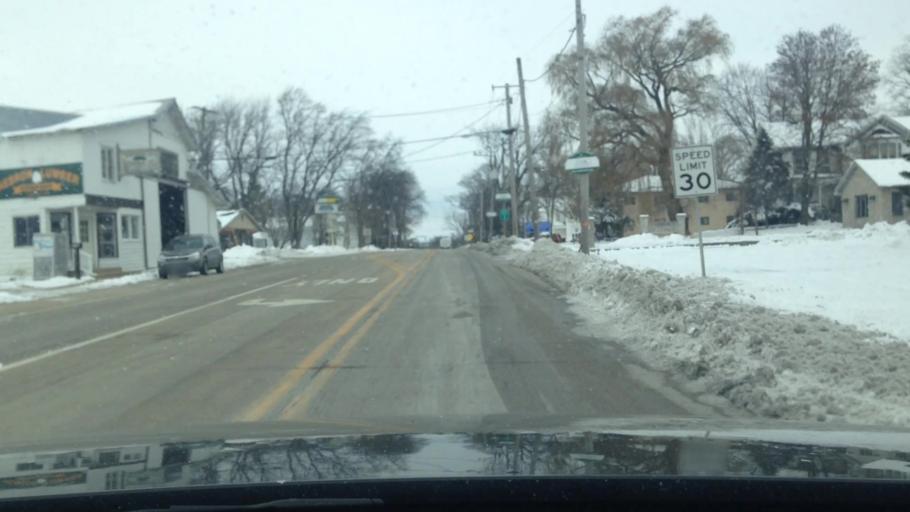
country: US
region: Illinois
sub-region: McHenry County
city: Hebron
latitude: 42.4722
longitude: -88.4327
